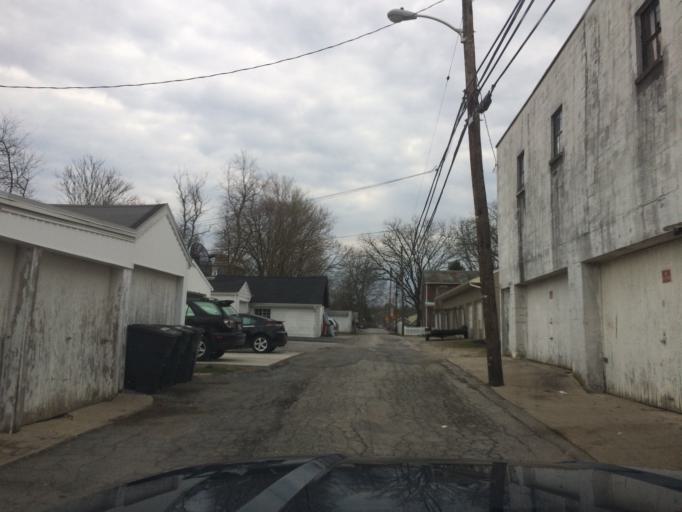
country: US
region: Maryland
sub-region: Carroll County
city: Westminster
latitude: 39.5712
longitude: -76.9950
